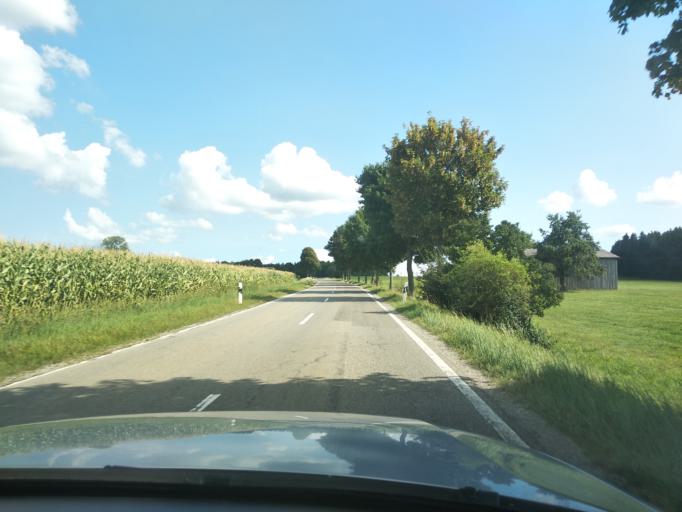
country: DE
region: Baden-Wuerttemberg
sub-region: Tuebingen Region
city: Leutkirch im Allgau
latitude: 47.8856
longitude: 9.9804
